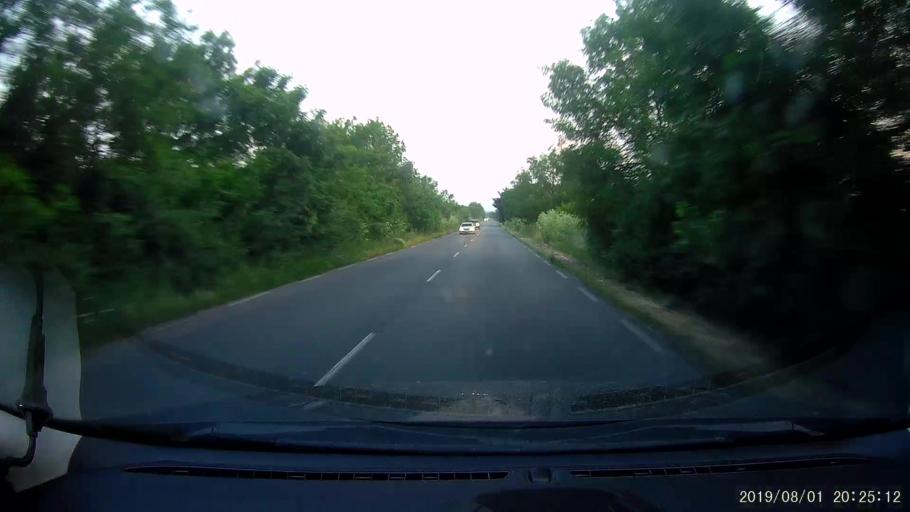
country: BG
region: Yambol
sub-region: Obshtina Elkhovo
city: Elkhovo
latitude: 42.2193
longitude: 26.5889
